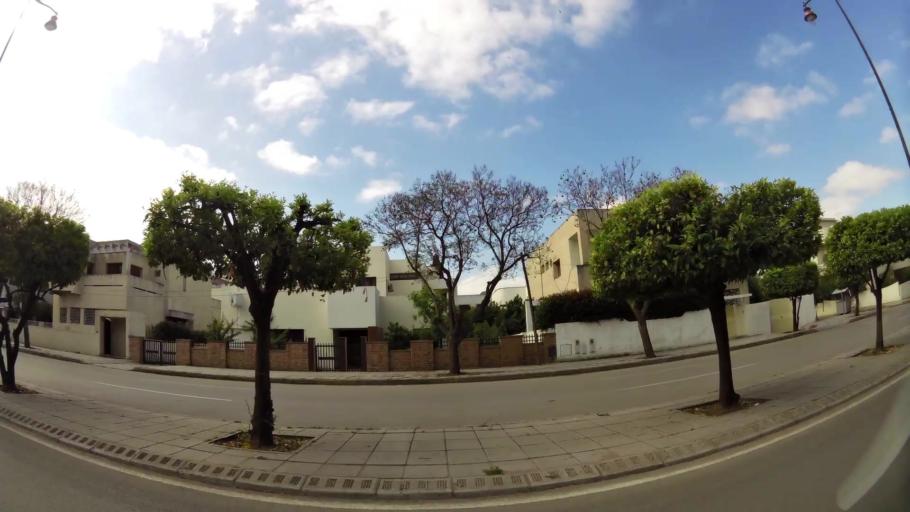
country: MA
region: Fes-Boulemane
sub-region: Fes
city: Fes
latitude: 34.0313
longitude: -5.0127
